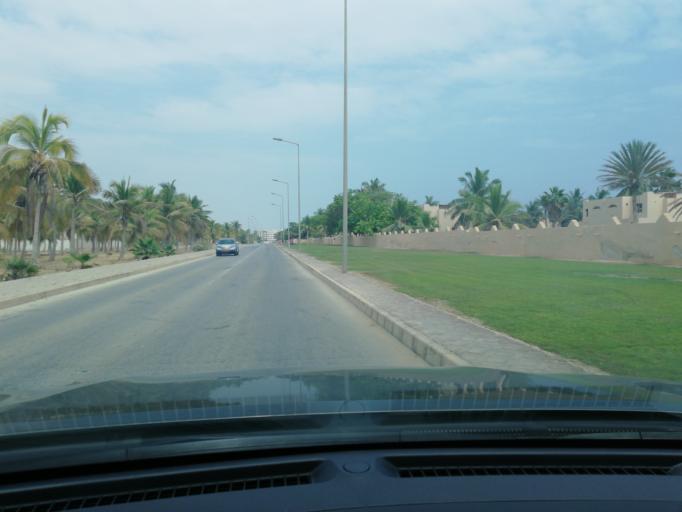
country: OM
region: Zufar
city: Salalah
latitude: 17.0090
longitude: 54.1478
